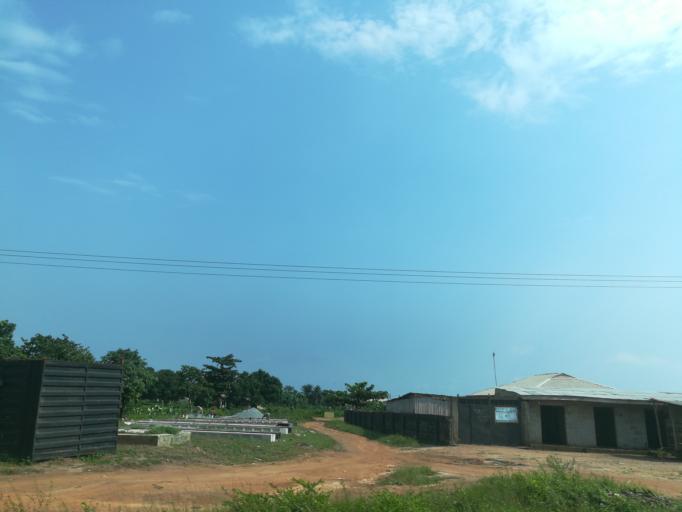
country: NG
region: Lagos
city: Ikorodu
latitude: 6.6077
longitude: 3.6310
